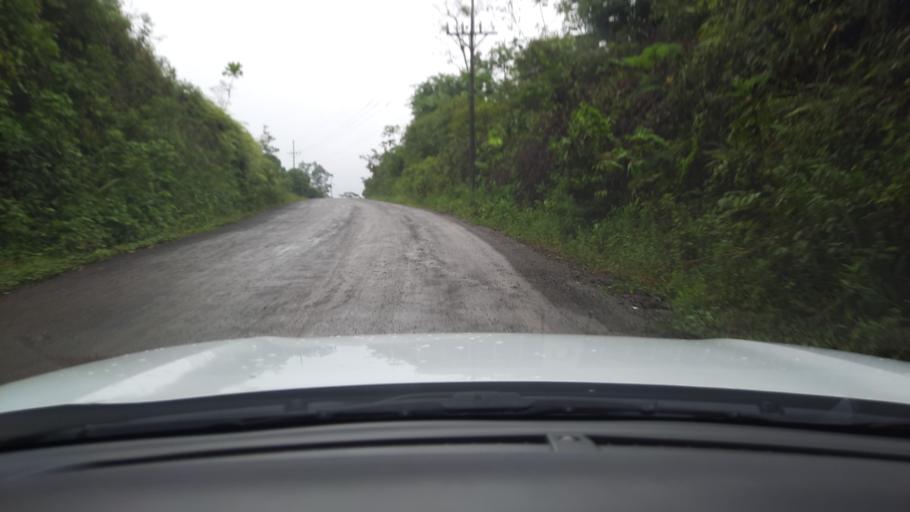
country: CR
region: Alajuela
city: San Jose
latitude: 11.0183
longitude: -85.3563
